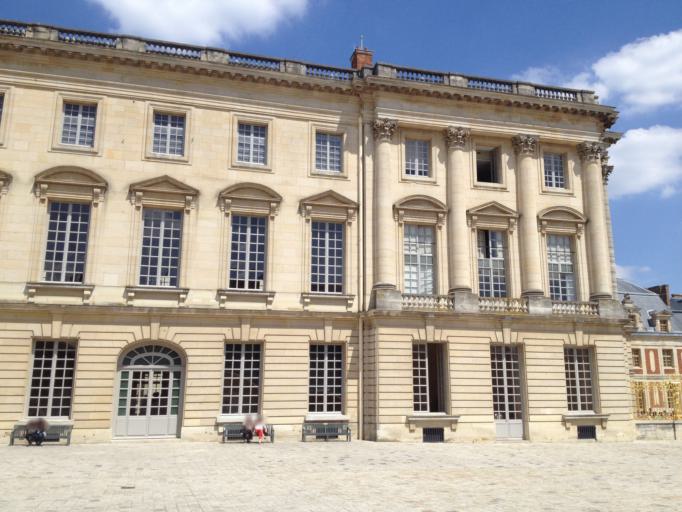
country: FR
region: Ile-de-France
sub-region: Departement des Yvelines
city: Versailles
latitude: 48.8045
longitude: 2.1217
